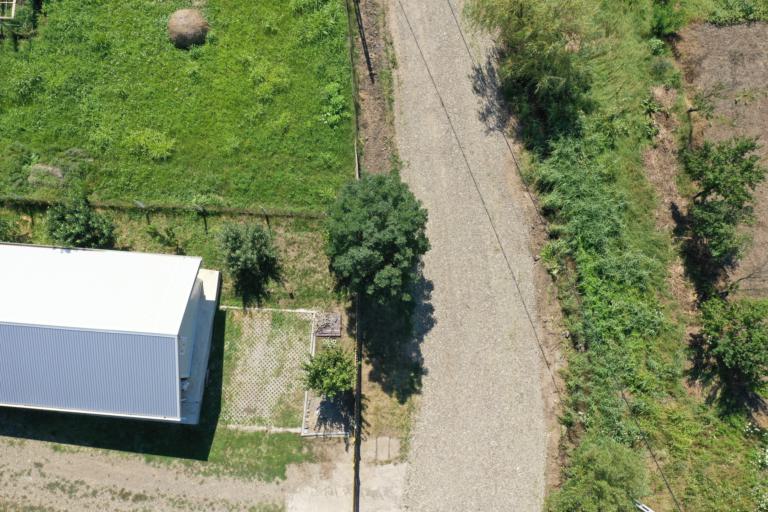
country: RO
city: Vanatori
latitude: 47.2532
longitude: 27.5216
